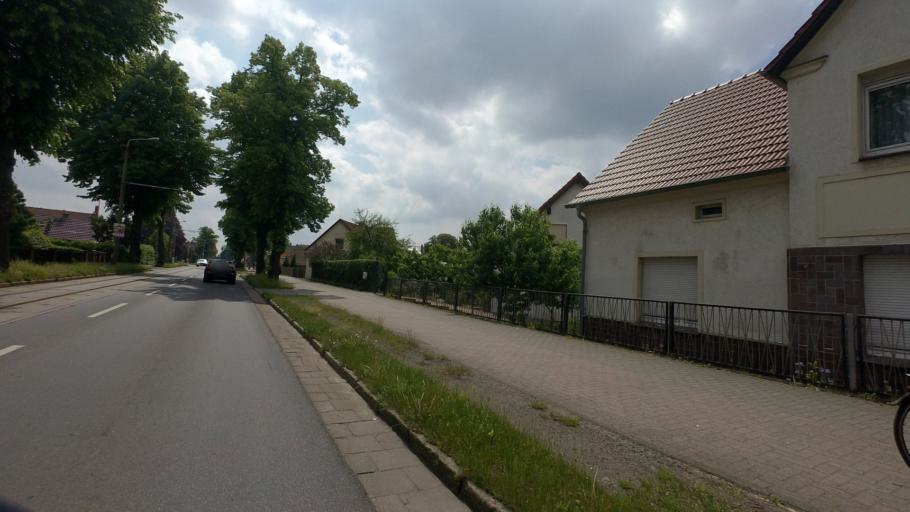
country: DE
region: Brandenburg
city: Cottbus
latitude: 51.7221
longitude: 14.3454
